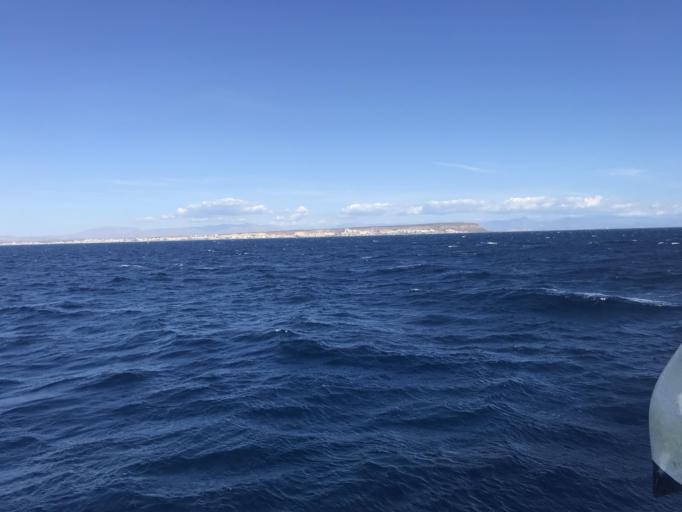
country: ES
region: Valencia
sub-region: Provincia de Alicante
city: Santa Pola
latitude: 38.1367
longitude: -0.5292
